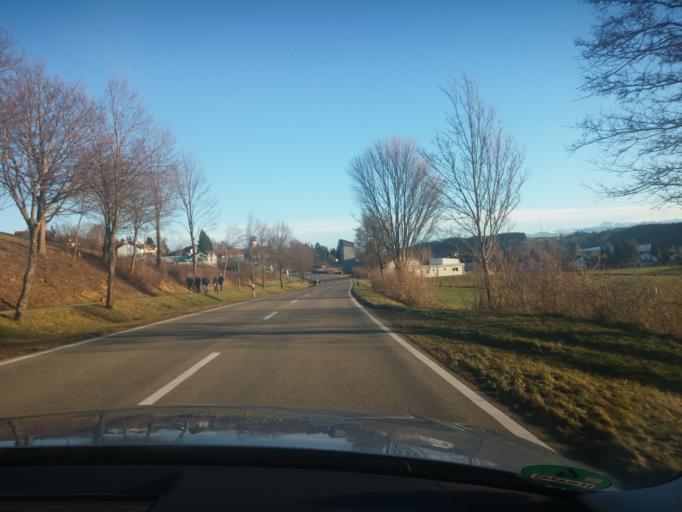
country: DE
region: Bavaria
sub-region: Swabia
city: Altusried
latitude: 47.8084
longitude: 10.2033
